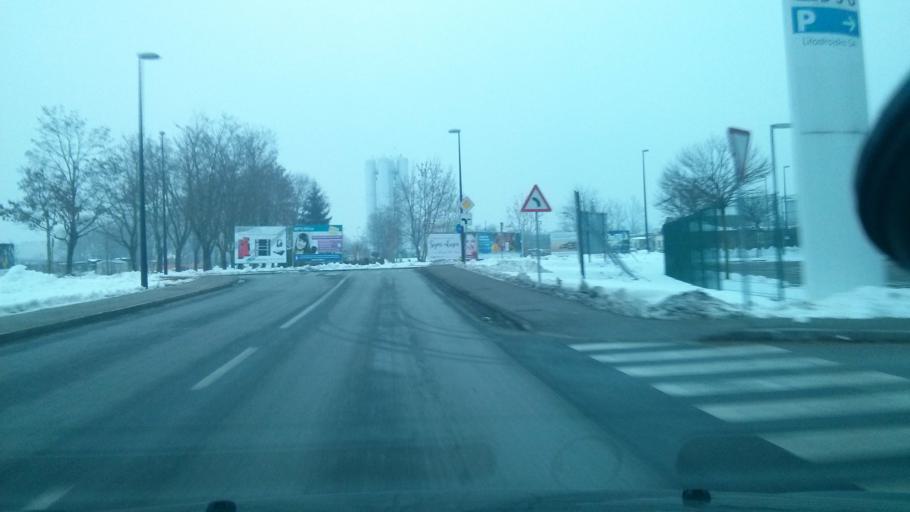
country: SI
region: Ljubljana
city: Ljubljana
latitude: 46.0822
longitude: 14.4970
